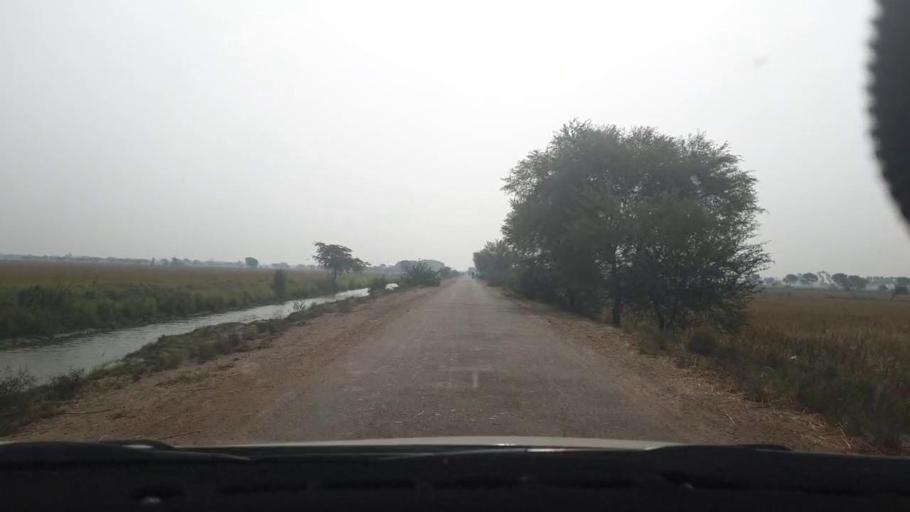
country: PK
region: Sindh
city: Tando Muhammad Khan
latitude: 25.0636
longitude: 68.5422
